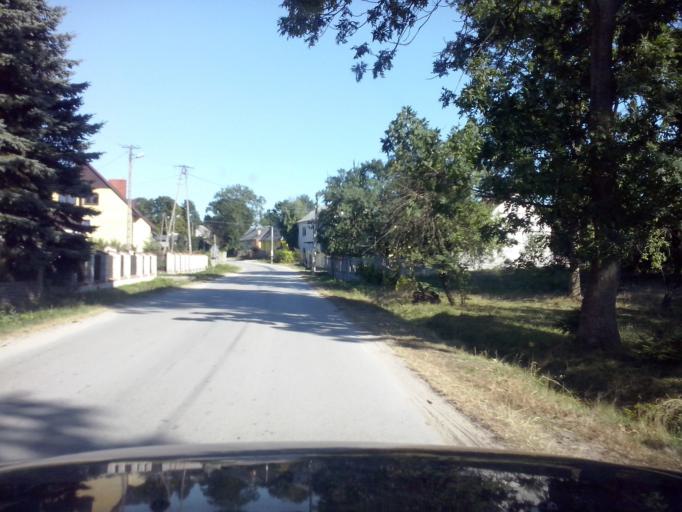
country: PL
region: Swietokrzyskie
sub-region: Powiat pinczowski
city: Kije
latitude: 50.5797
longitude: 20.6553
